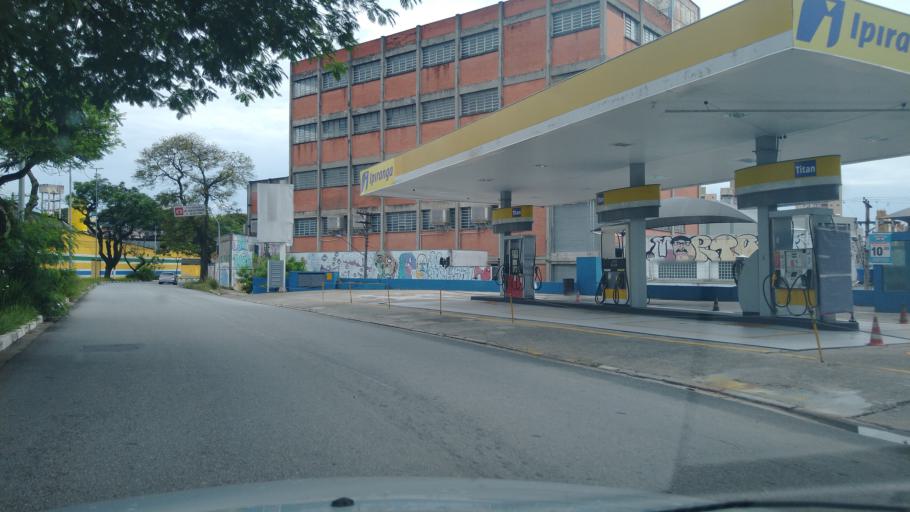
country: BR
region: Sao Paulo
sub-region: Guarulhos
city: Guarulhos
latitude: -23.4797
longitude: -46.5368
